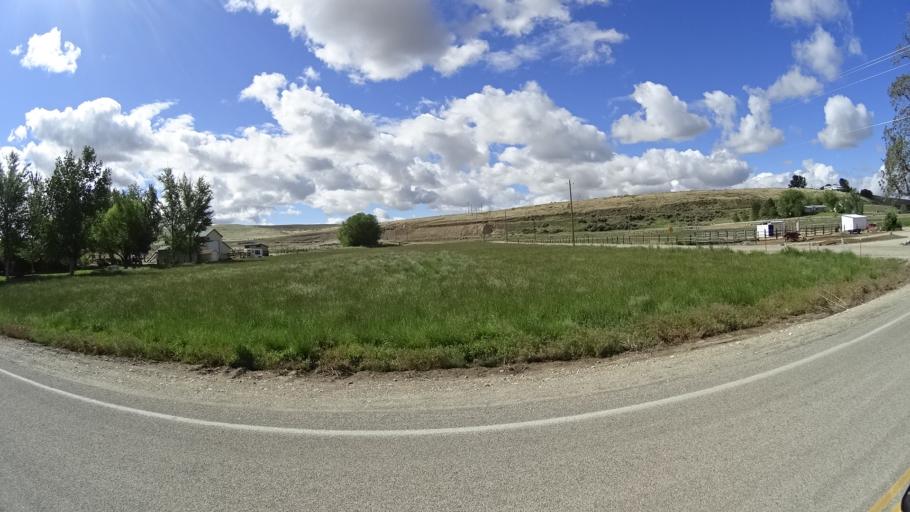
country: US
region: Idaho
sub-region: Ada County
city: Kuna
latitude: 43.4630
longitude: -116.4731
